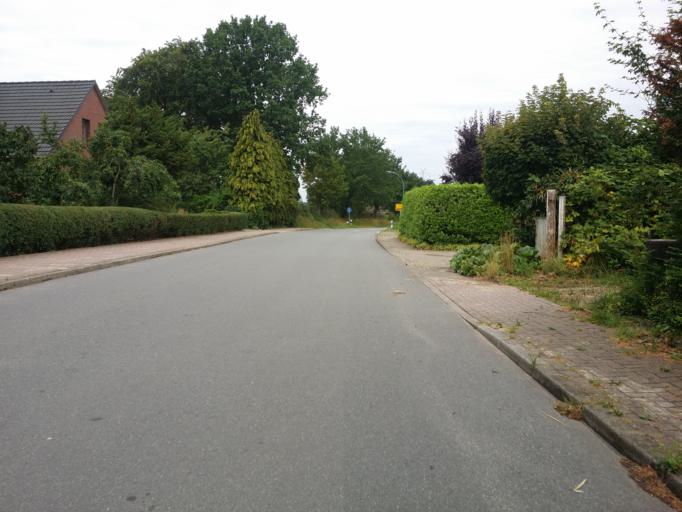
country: DE
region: Schleswig-Holstein
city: Oldendorf
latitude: 53.9588
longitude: 9.4501
